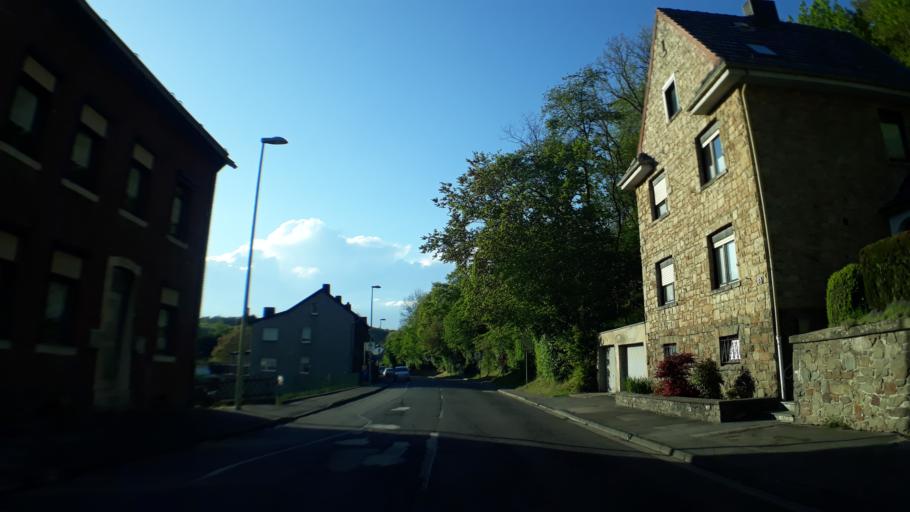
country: DE
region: North Rhine-Westphalia
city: Stolberg
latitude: 50.7163
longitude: 6.2622
